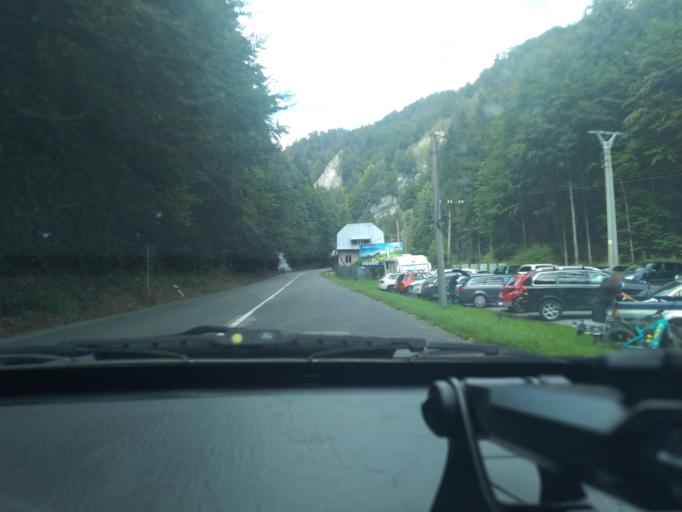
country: SK
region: Banskobystricky
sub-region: Okres Banska Bystrica
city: Banska Bystrica
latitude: 48.8187
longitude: 19.0382
